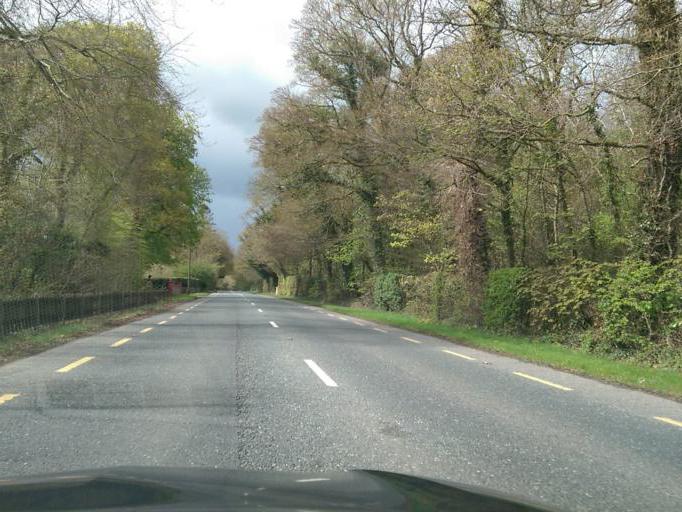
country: IE
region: Leinster
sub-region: An Mhi
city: Dunshaughlin
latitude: 53.5343
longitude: -6.5613
